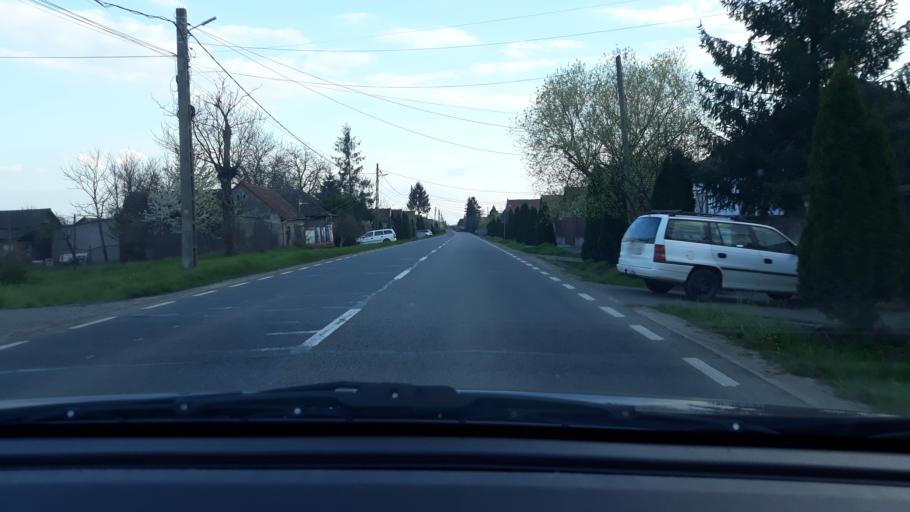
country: RO
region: Bihor
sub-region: Comuna Tamaseu
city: Tamaseu
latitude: 47.2016
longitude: 21.9197
